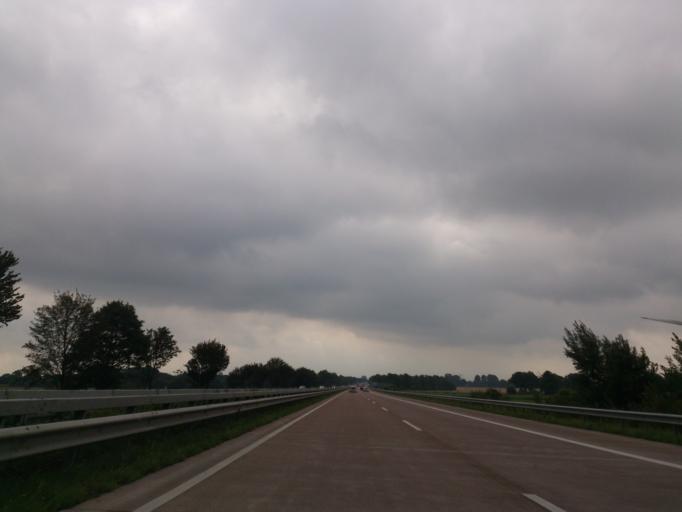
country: DE
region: Schleswig-Holstein
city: Hohenfelde
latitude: 53.8342
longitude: 9.6212
